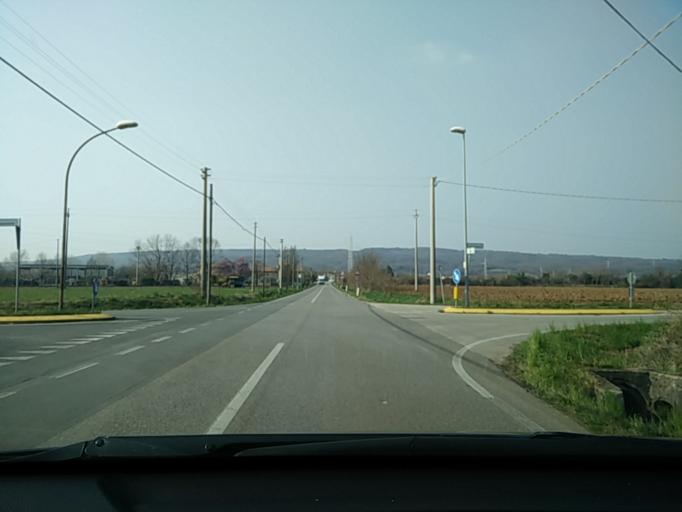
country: IT
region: Veneto
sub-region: Provincia di Treviso
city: Selva del Montello
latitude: 45.7744
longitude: 12.1412
